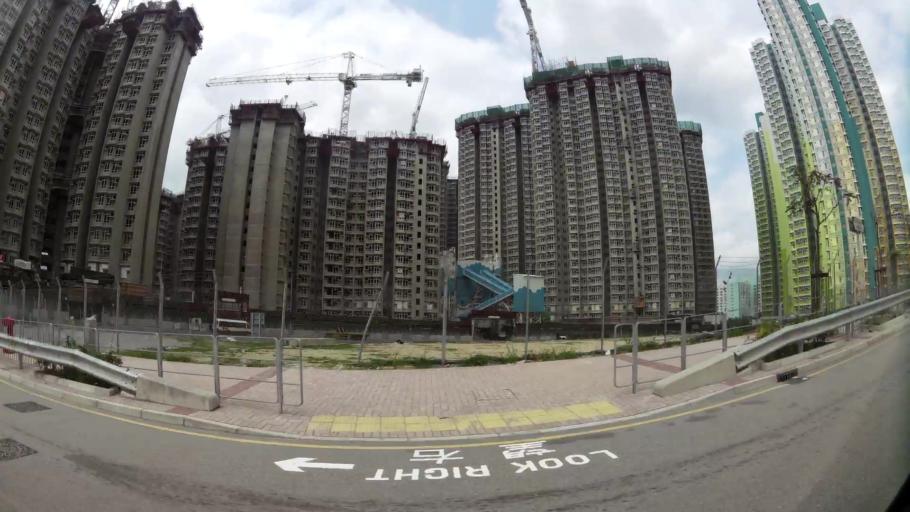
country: HK
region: Kowloon City
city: Kowloon
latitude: 22.3281
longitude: 114.2302
